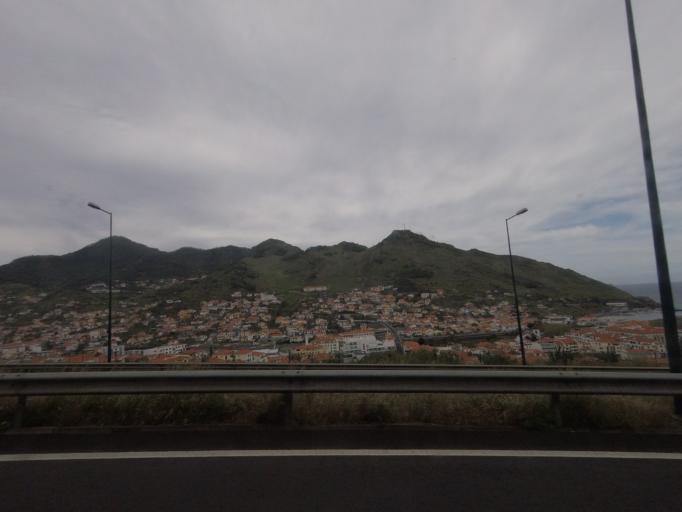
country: PT
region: Madeira
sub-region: Machico
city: Machico
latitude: 32.7176
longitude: -16.7709
